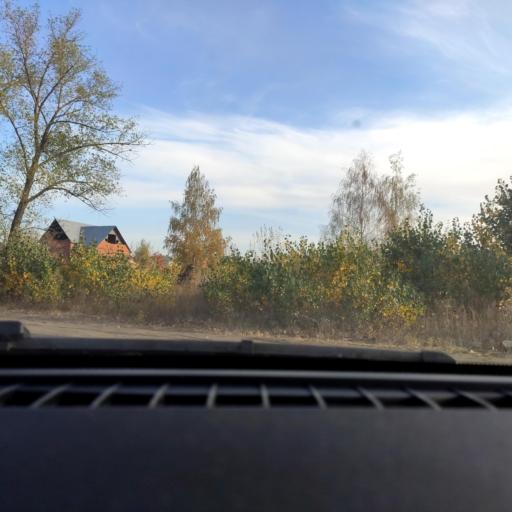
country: RU
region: Voronezj
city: Somovo
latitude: 51.6717
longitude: 39.3242
